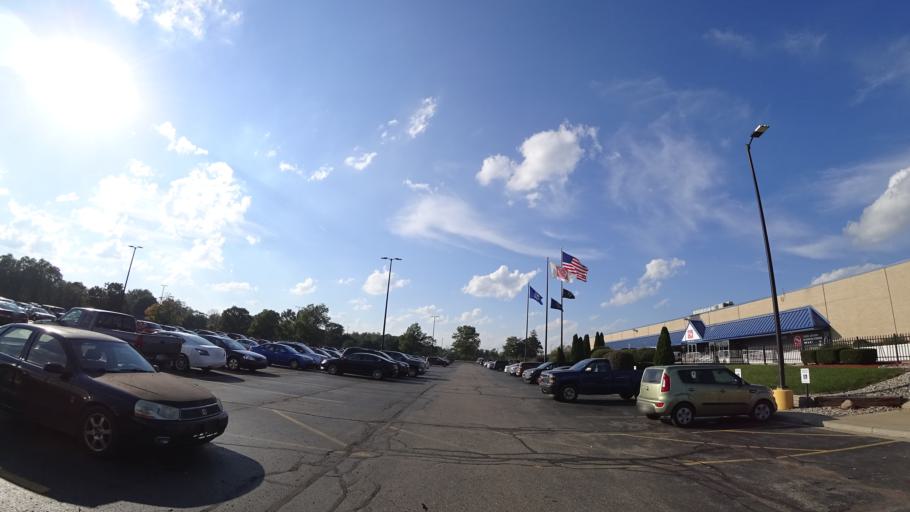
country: US
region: Michigan
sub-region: Saint Joseph County
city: Three Rivers
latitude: 41.9558
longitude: -85.6421
